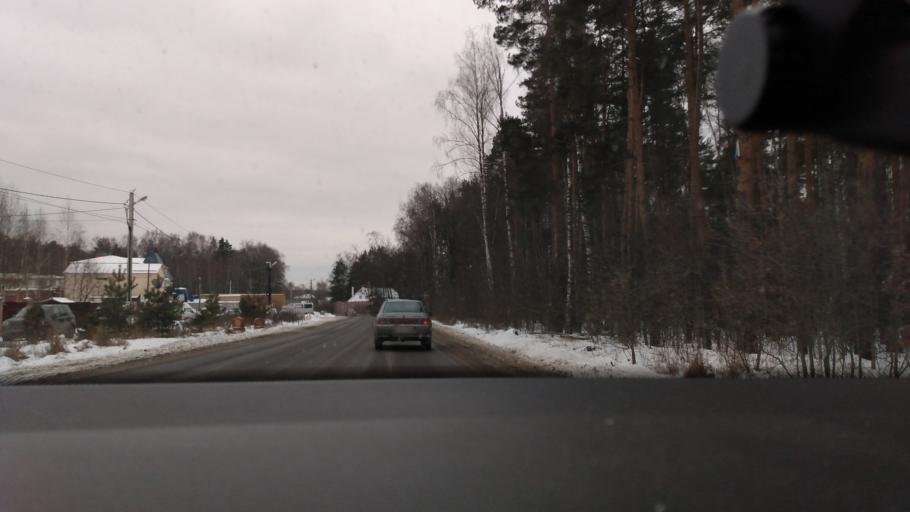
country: RU
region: Moskovskaya
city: Bykovo
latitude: 55.6624
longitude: 38.1020
